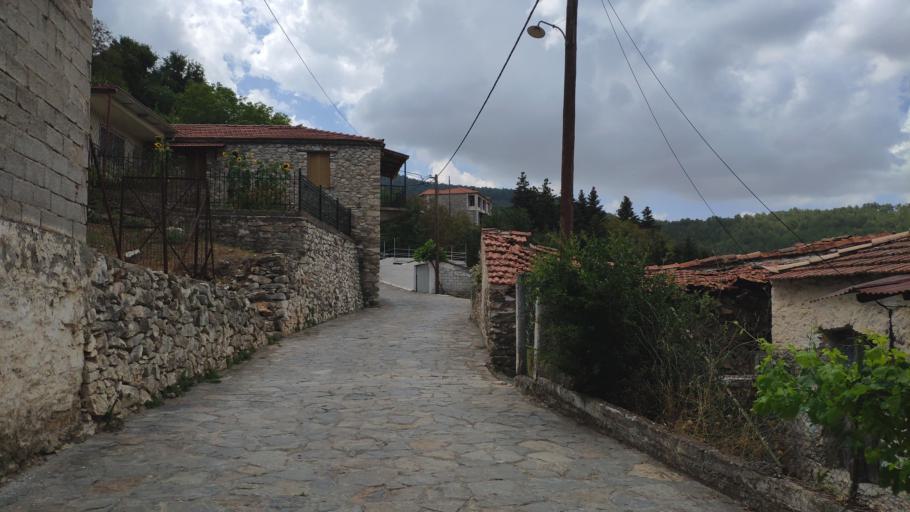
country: GR
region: Peloponnese
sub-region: Nomos Lakonias
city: Kariai
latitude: 37.2447
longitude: 22.5516
